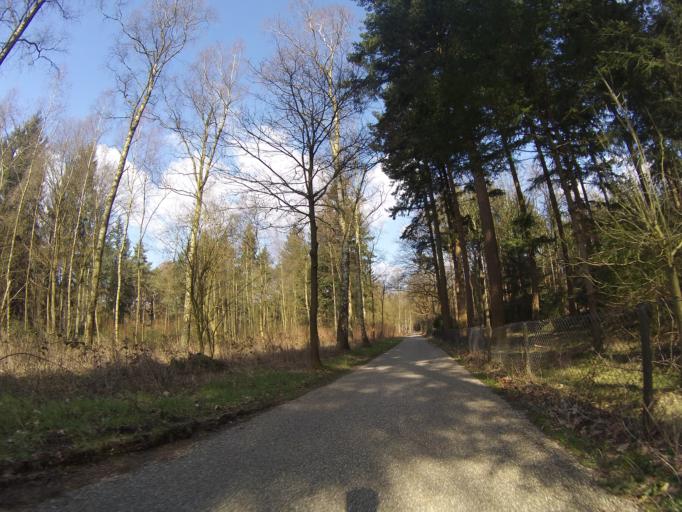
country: NL
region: Utrecht
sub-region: Gemeente Soest
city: Soest
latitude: 52.1425
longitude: 5.2770
